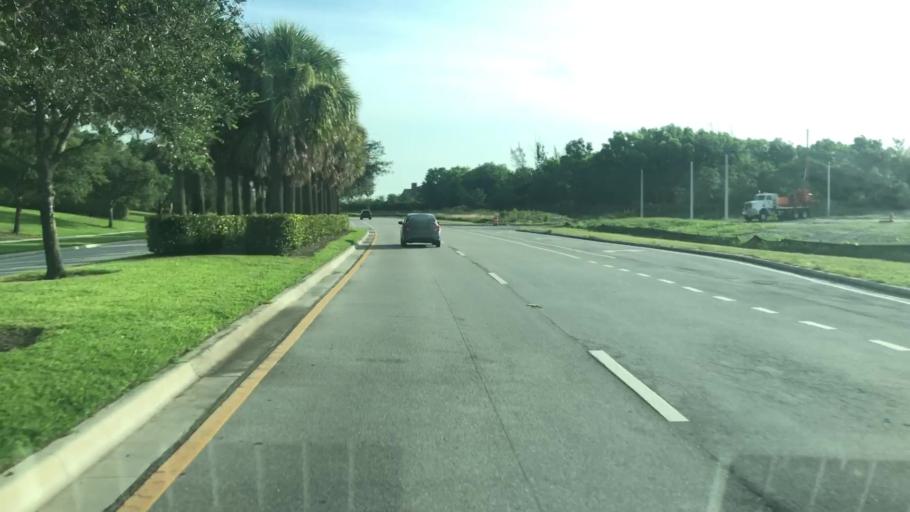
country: US
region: Florida
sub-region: Broward County
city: Parkland
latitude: 26.3152
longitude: -80.2517
